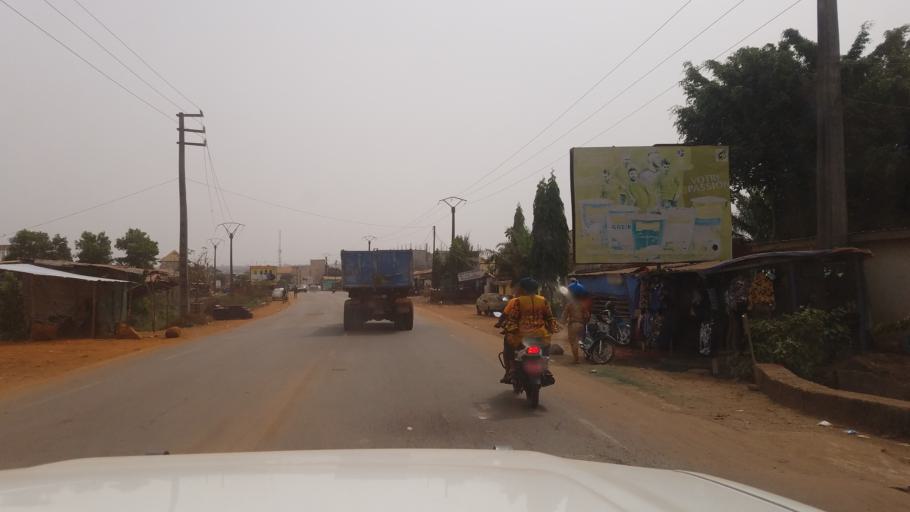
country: GN
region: Kindia
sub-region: Prefecture de Dubreka
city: Dubreka
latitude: 9.6803
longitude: -13.5791
